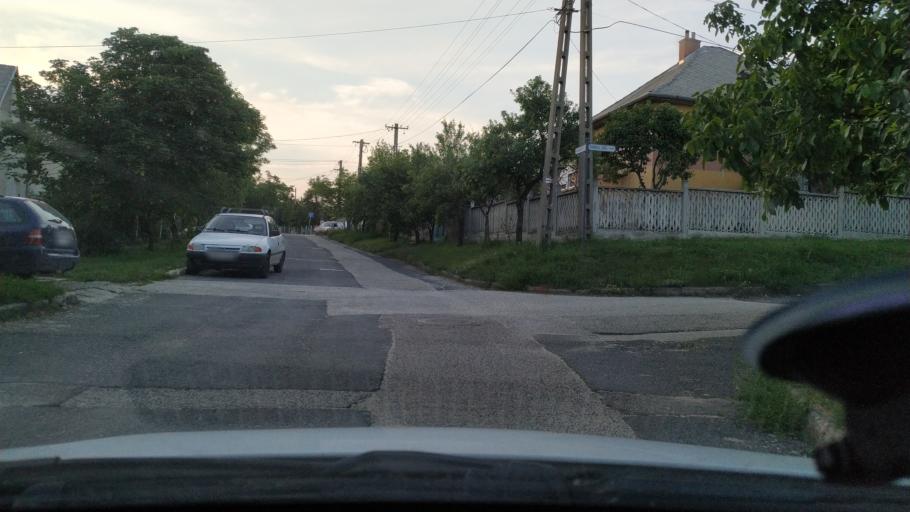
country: HU
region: Veszprem
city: Varpalota
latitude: 47.2036
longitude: 18.1798
